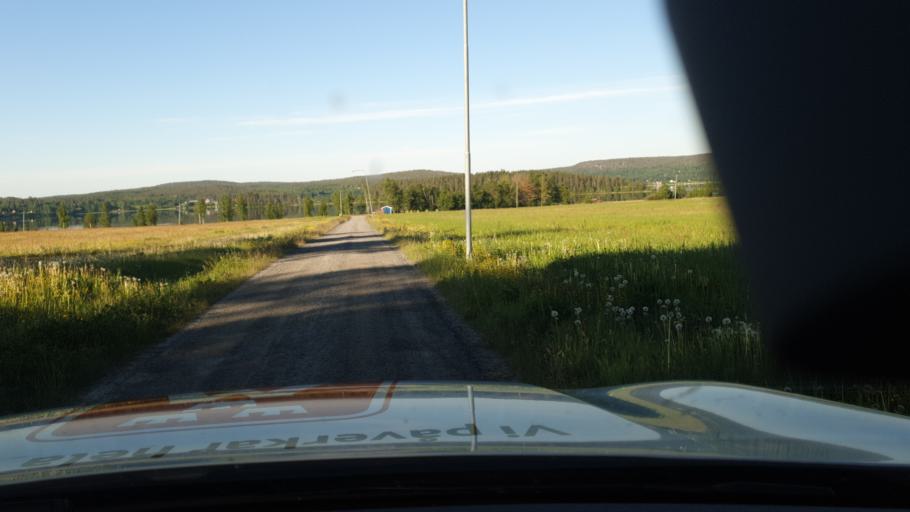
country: SE
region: Vaesterbotten
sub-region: Umea Kommun
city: Roback
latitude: 64.0043
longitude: 20.0843
